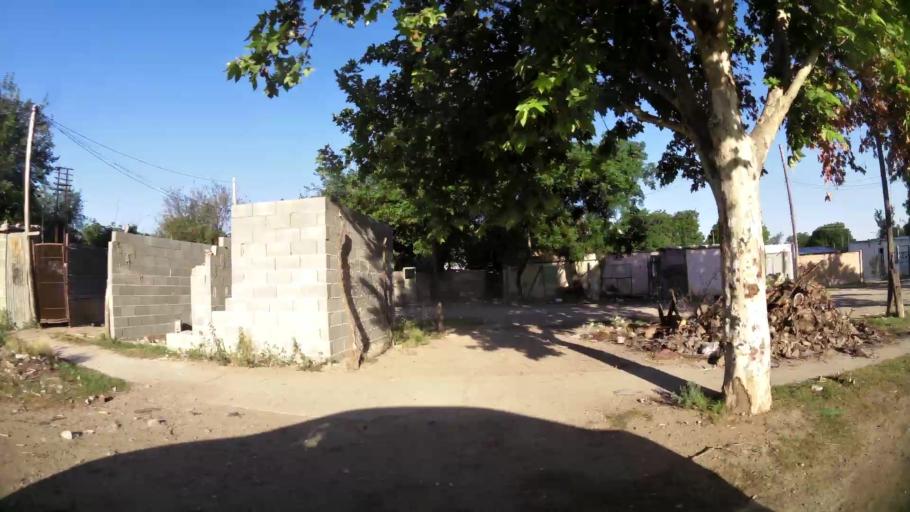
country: AR
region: Cordoba
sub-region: Departamento de Capital
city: Cordoba
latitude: -31.3763
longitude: -64.1899
